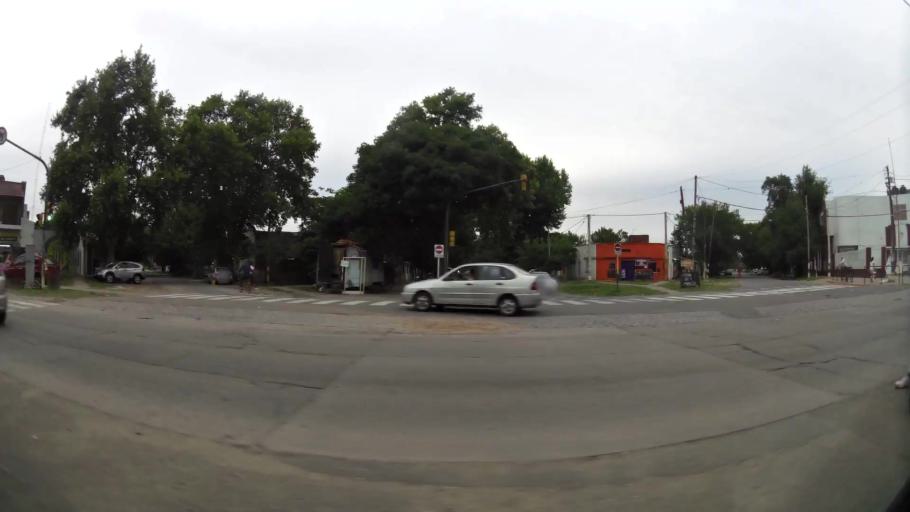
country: AR
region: Santa Fe
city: Granadero Baigorria
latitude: -32.9047
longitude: -60.6992
